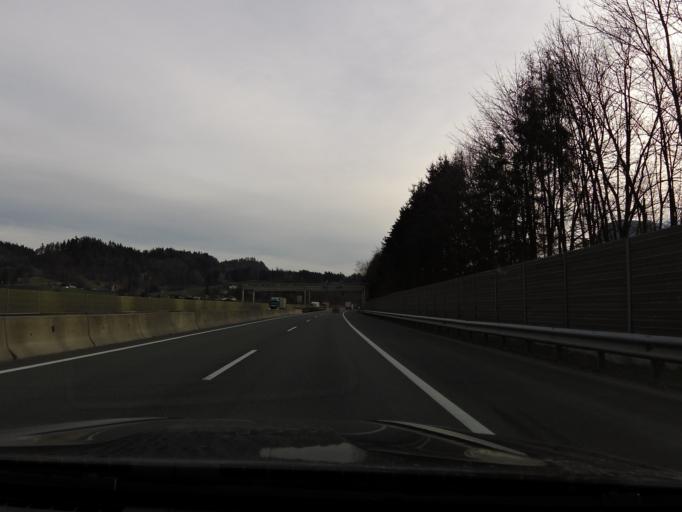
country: AT
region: Tyrol
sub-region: Politischer Bezirk Kufstein
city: Kufstein
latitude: 47.5827
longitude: 12.1523
